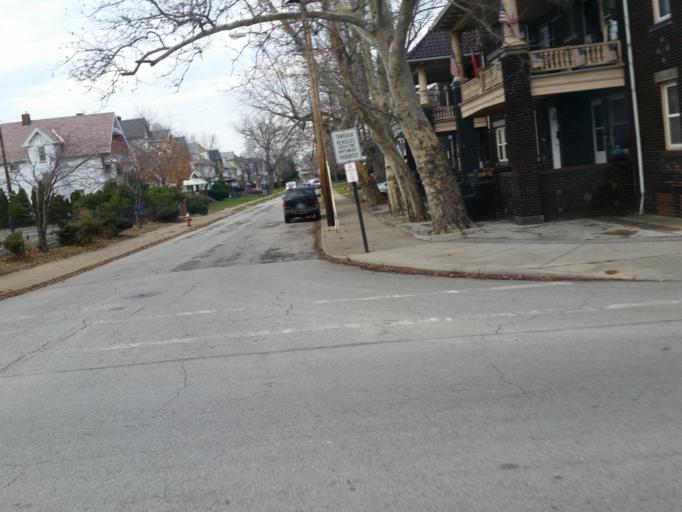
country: US
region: Ohio
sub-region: Cuyahoga County
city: East Cleveland
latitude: 41.5414
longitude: -81.6018
